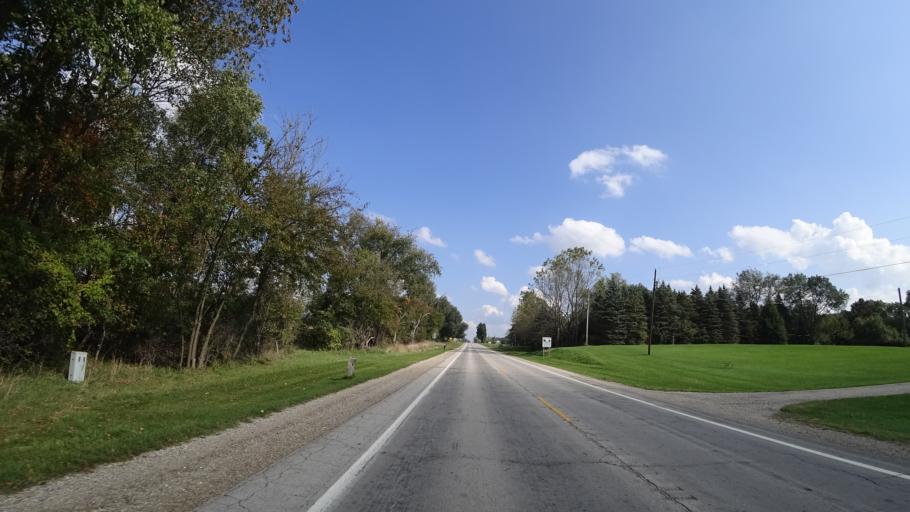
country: US
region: Michigan
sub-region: Saint Joseph County
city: Colon
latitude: 42.0102
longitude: -85.4085
